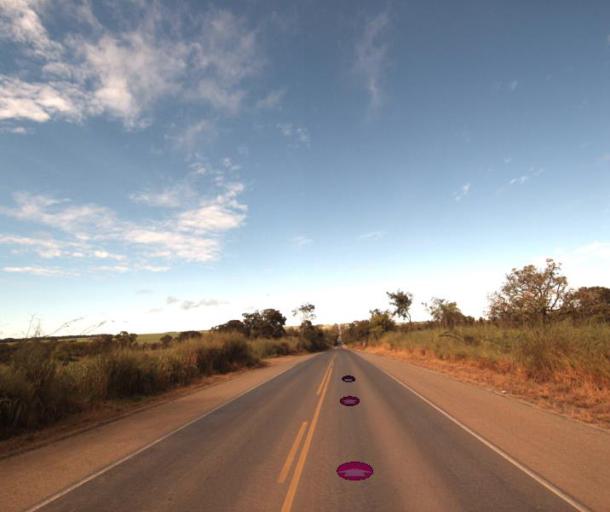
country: BR
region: Goias
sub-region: Itapaci
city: Itapaci
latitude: -14.8078
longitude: -49.2896
